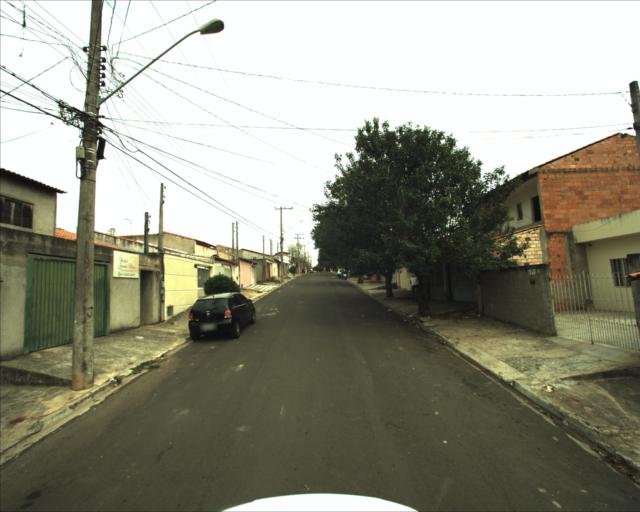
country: BR
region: Sao Paulo
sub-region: Sorocaba
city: Sorocaba
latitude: -23.4957
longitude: -47.5270
